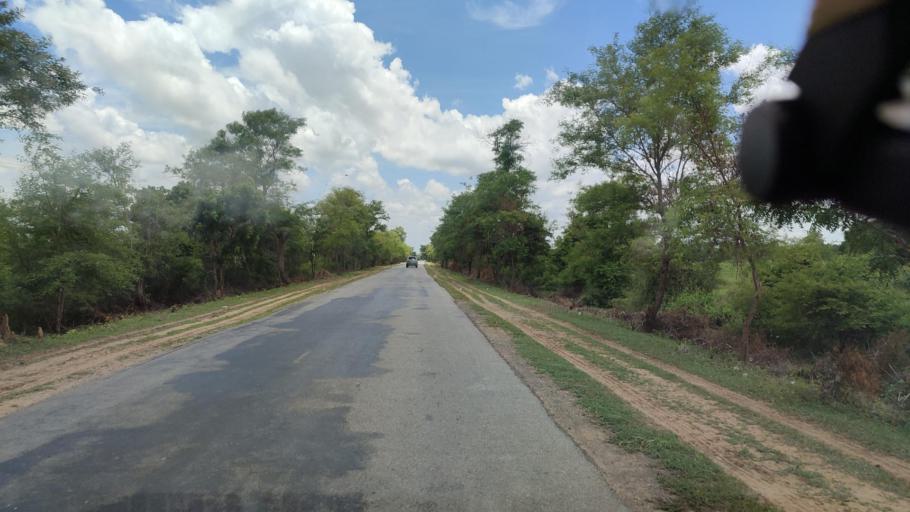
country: MM
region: Magway
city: Taungdwingyi
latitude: 20.1962
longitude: 95.3882
